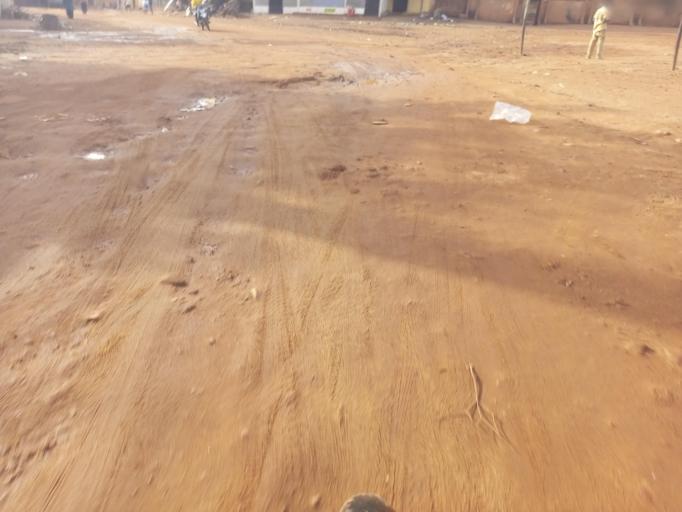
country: ML
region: Bamako
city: Bamako
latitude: 12.6004
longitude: -7.9884
